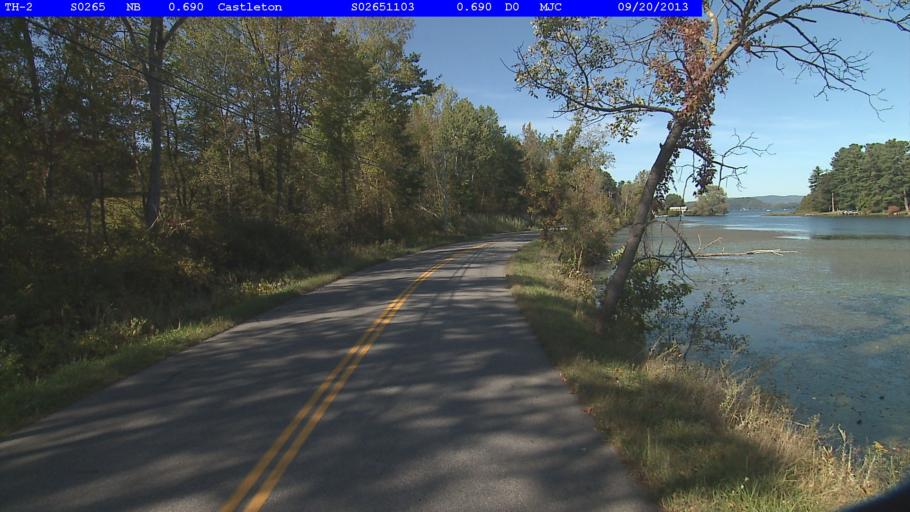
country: US
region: Vermont
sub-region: Rutland County
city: Fair Haven
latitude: 43.6142
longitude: -73.2317
